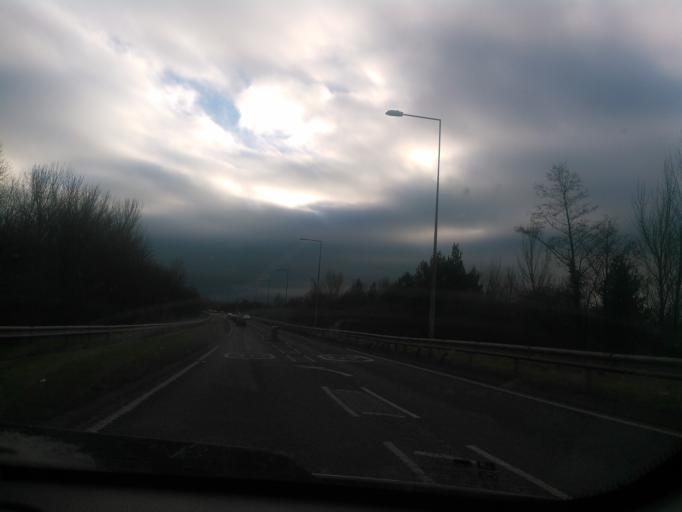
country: GB
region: England
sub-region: Telford and Wrekin
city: Oakengates
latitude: 52.7030
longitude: -2.4606
